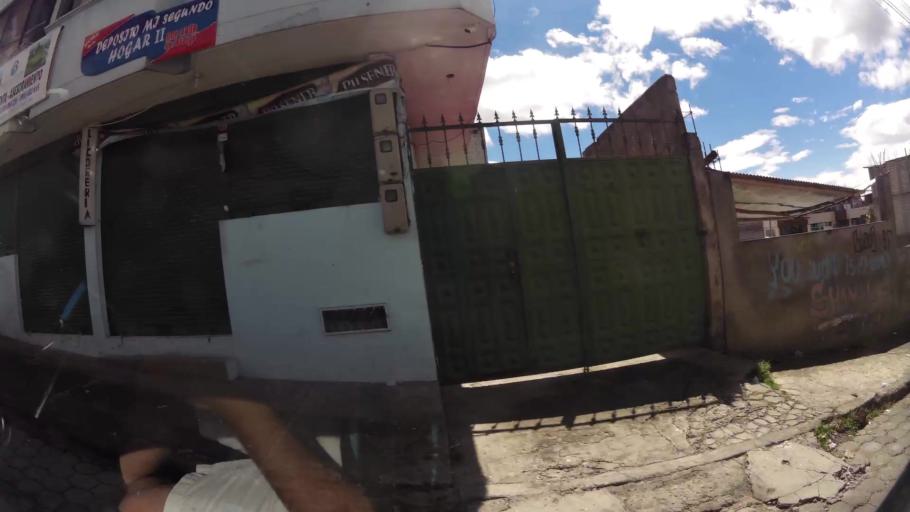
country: EC
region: Pichincha
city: Sangolqui
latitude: -0.3323
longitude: -78.5594
